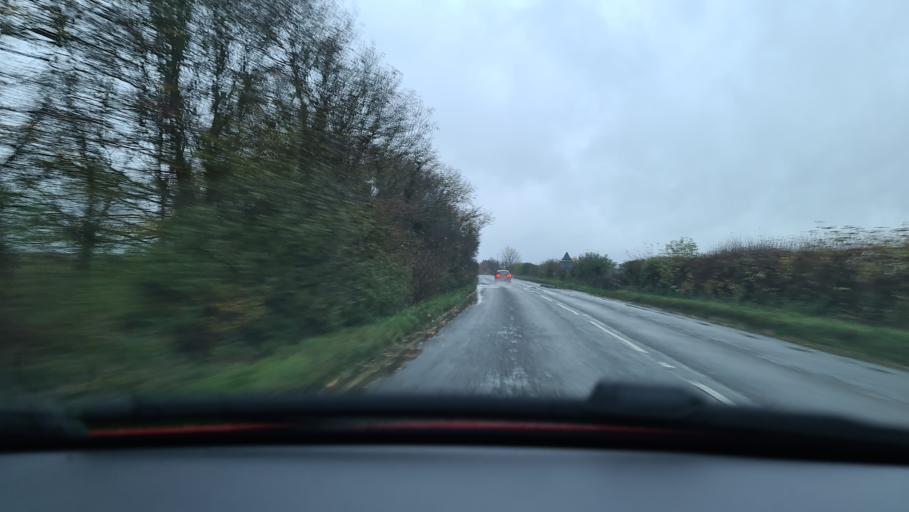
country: GB
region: England
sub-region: Oxfordshire
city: Somerton
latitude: 51.9355
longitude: -1.2152
